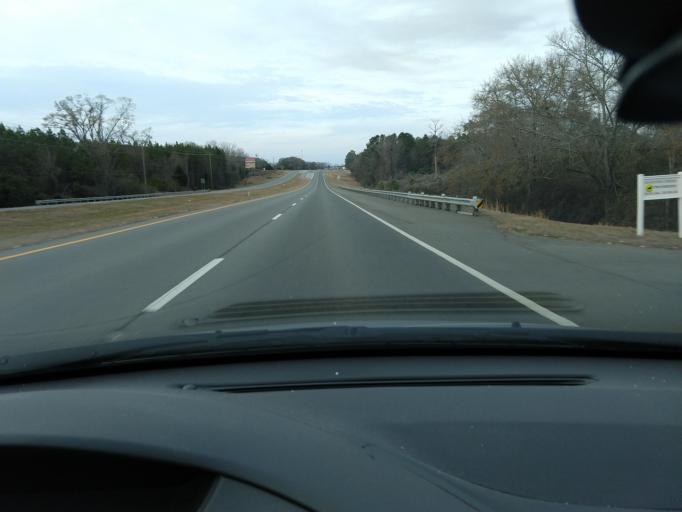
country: US
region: Georgia
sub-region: Sumter County
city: Americus
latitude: 32.0508
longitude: -84.2538
